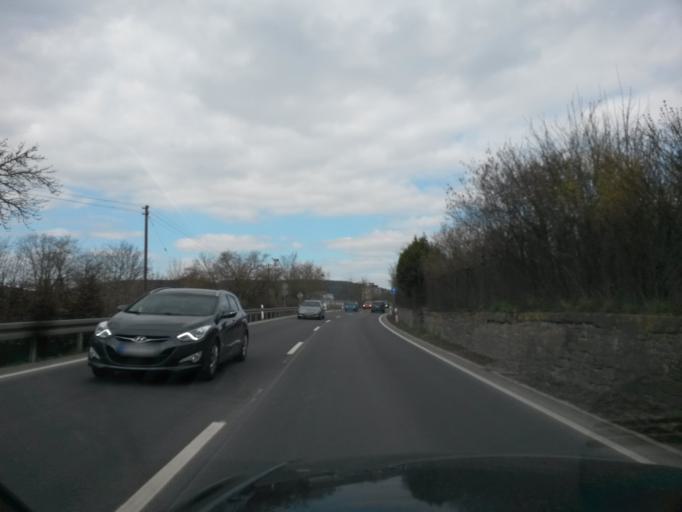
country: DE
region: Bavaria
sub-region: Regierungsbezirk Unterfranken
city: Wuerzburg
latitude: 49.7703
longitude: 9.9485
